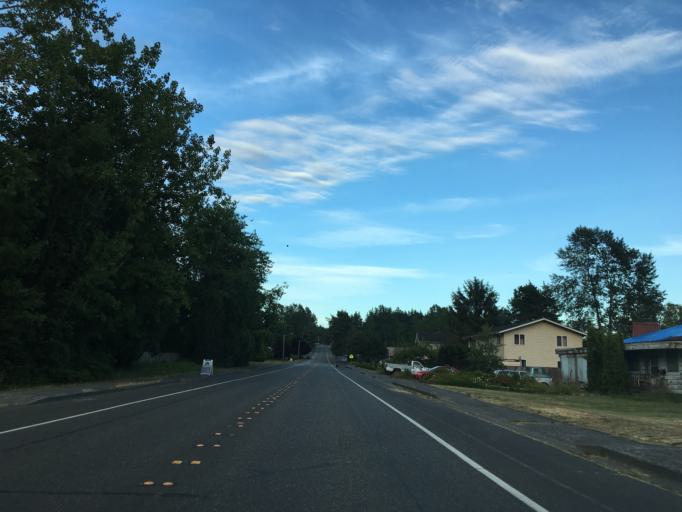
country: US
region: Washington
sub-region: Whatcom County
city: Blaine
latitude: 48.9981
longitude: -122.7423
